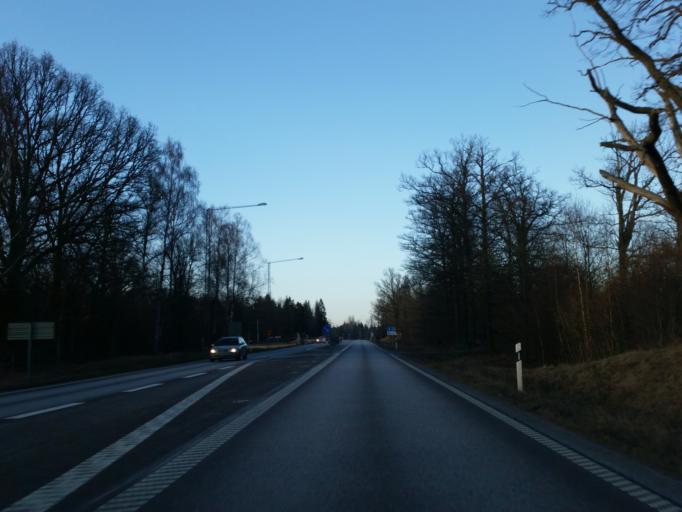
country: SE
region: Kalmar
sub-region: Oskarshamns Kommun
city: Oskarshamn
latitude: 57.3397
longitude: 16.4855
